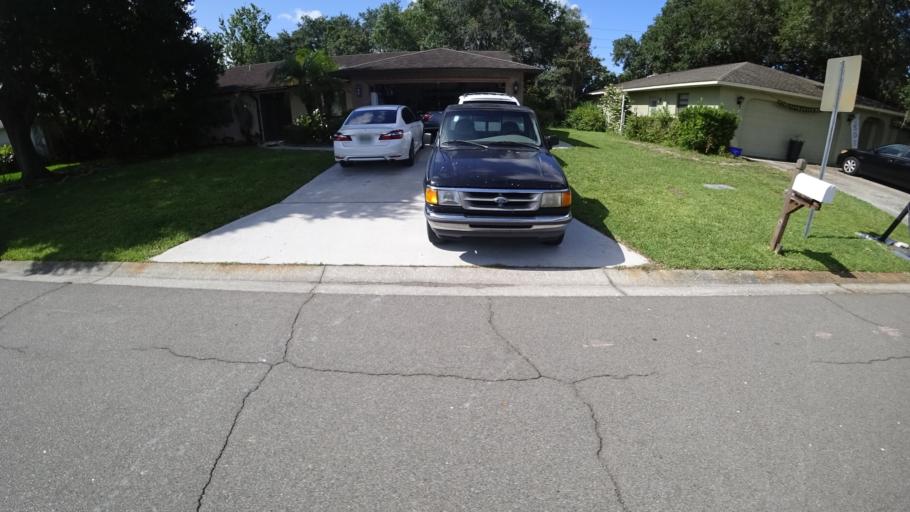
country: US
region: Florida
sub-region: Sarasota County
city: Desoto Lakes
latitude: 27.3891
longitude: -82.4981
